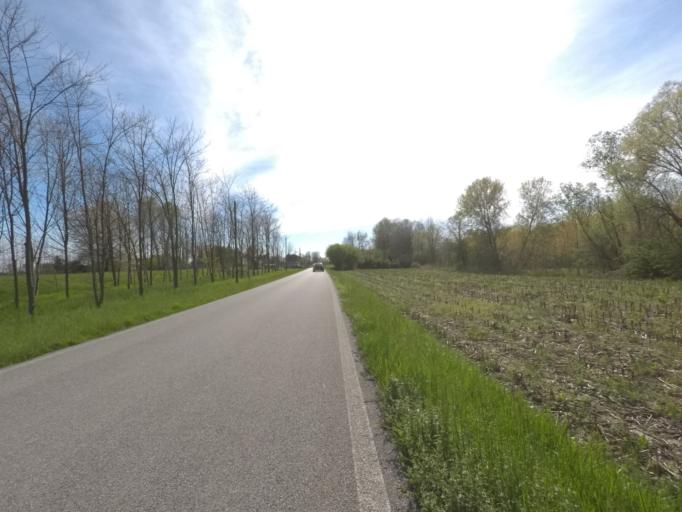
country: IT
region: Friuli Venezia Giulia
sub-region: Provincia di Pordenone
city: Azzano Decimo
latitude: 45.9311
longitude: 12.6934
